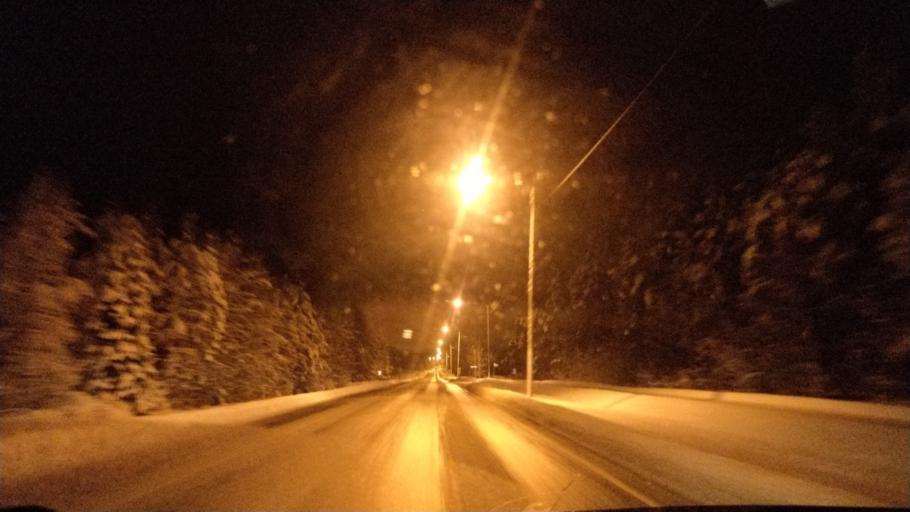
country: FI
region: Lapland
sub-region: Rovaniemi
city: Rovaniemi
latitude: 66.2971
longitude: 25.3522
